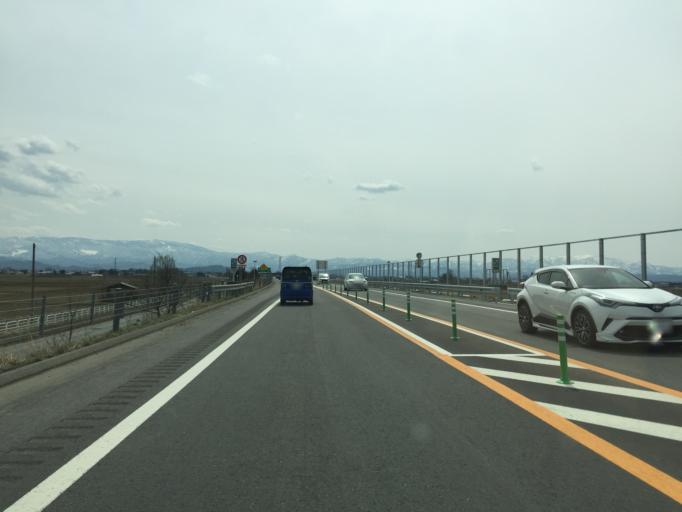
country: JP
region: Yamagata
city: Takahata
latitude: 38.0193
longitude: 140.1590
